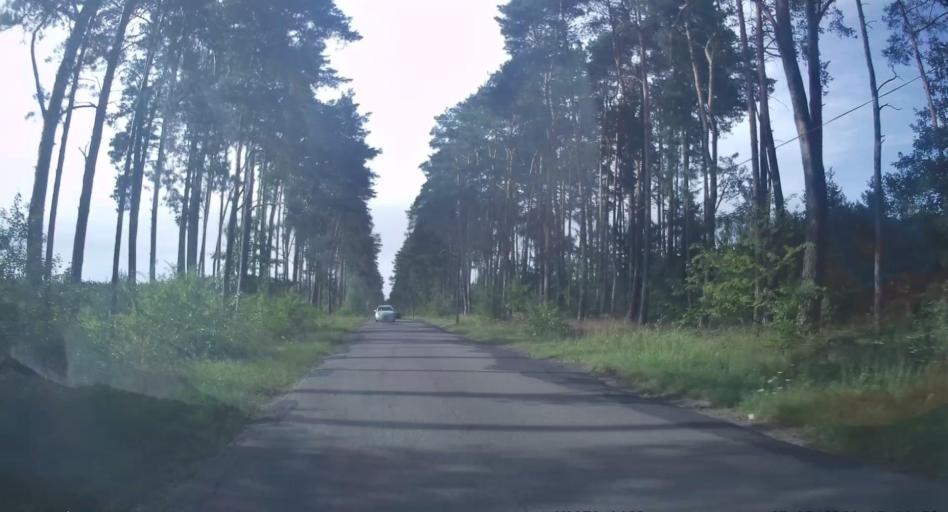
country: PL
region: Swietokrzyskie
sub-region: Powiat konecki
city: Konskie
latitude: 51.2213
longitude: 20.3879
